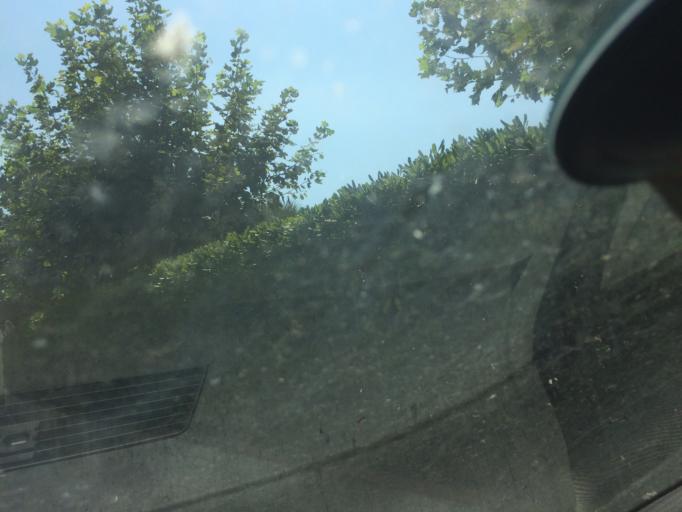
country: IT
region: Tuscany
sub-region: Provincia di Massa-Carrara
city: Massa
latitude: 44.0207
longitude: 10.0897
